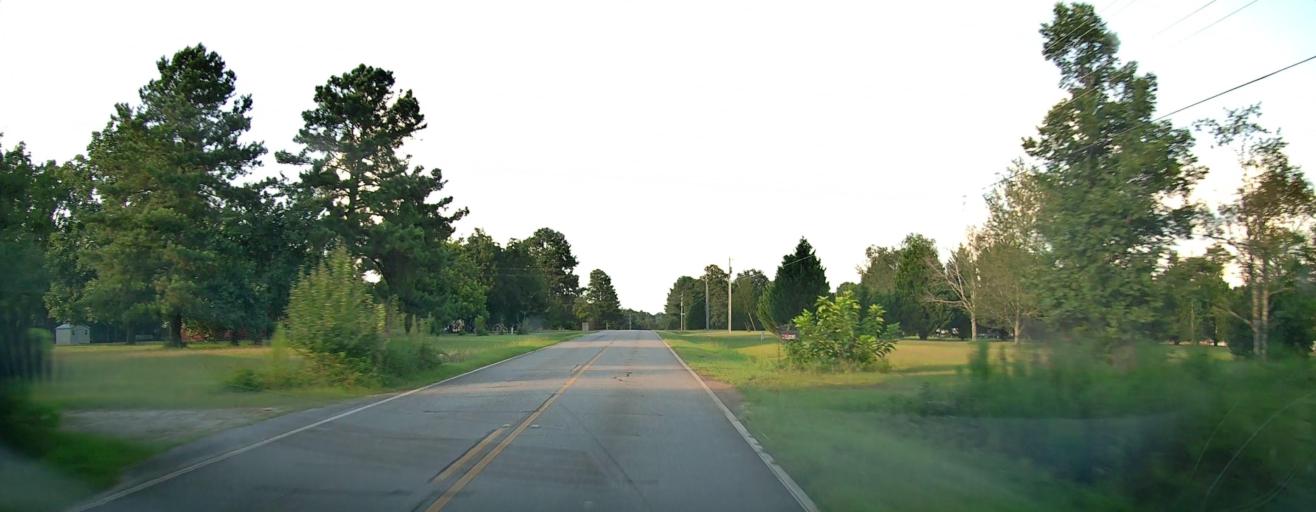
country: US
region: Georgia
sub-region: Peach County
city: Byron
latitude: 32.6186
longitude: -83.8288
